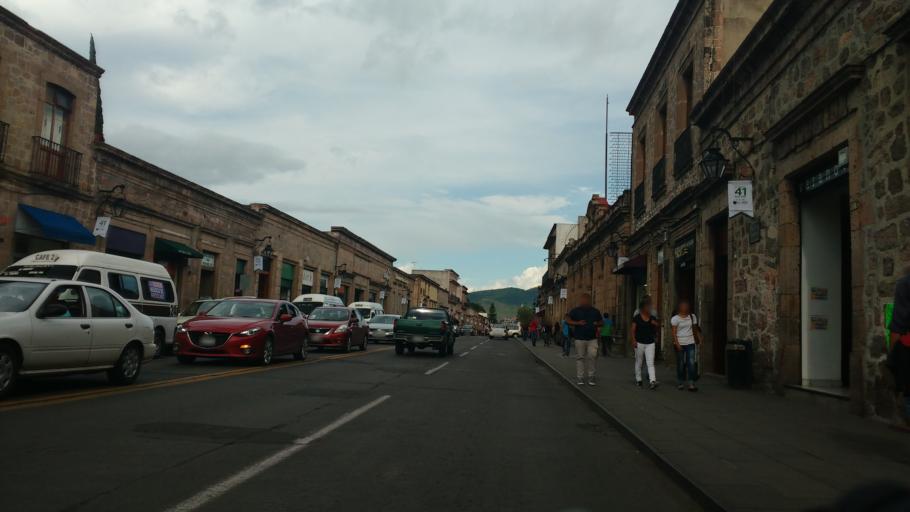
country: MX
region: Michoacan
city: Morelia
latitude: 19.7028
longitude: -101.1862
